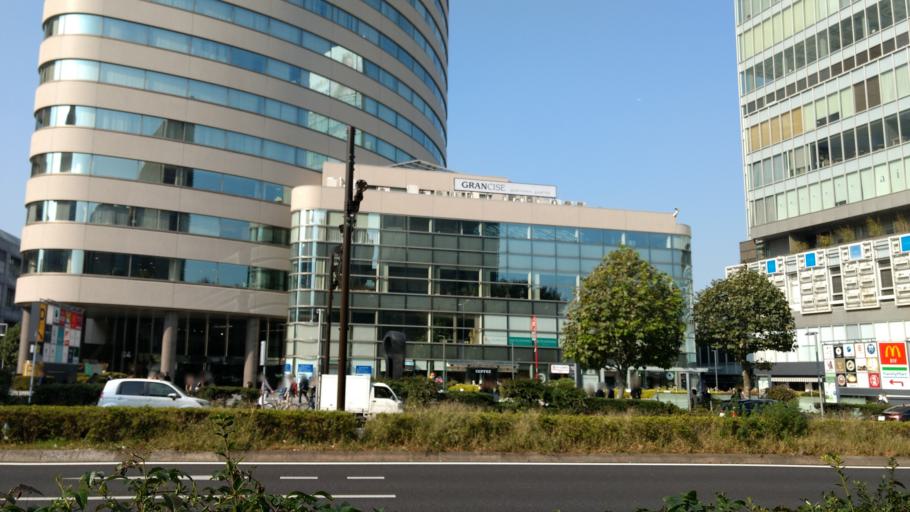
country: JP
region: Tokyo
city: Tokyo
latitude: 35.6622
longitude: 139.7094
